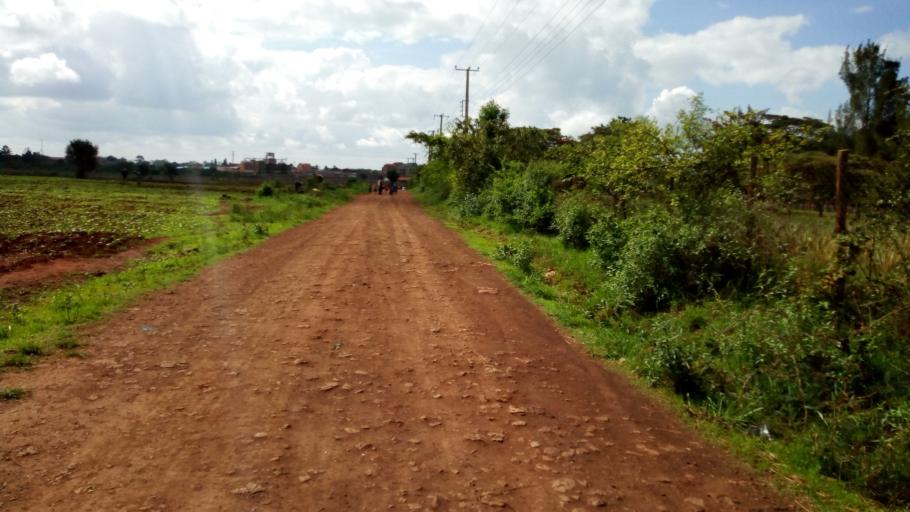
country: KE
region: Nairobi Area
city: Thika
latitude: -1.0558
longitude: 37.1204
